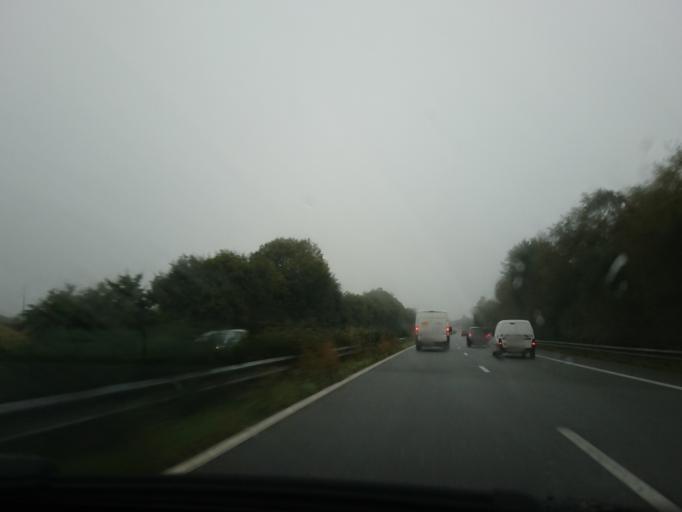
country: FR
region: Brittany
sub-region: Departement du Finistere
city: Saint-Yvi
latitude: 47.9564
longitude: -3.9515
